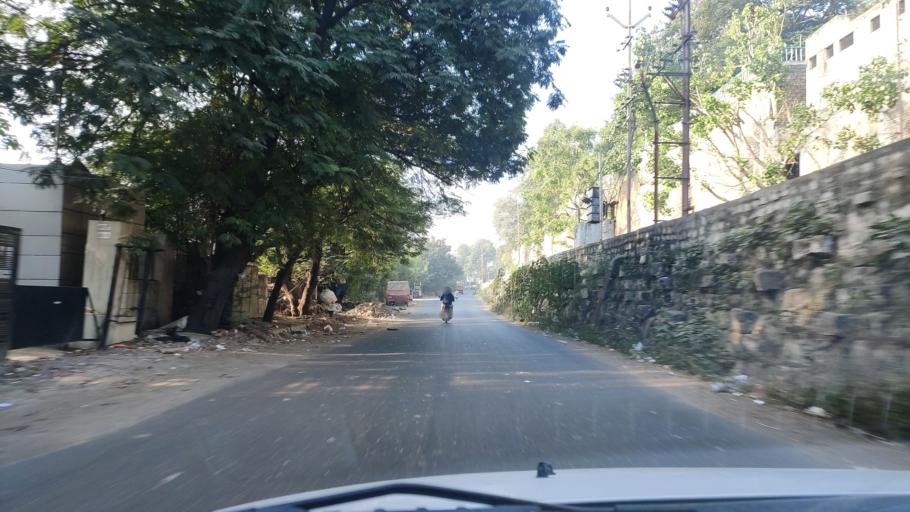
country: IN
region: Telangana
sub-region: Hyderabad
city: Hyderabad
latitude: 17.4150
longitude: 78.4799
